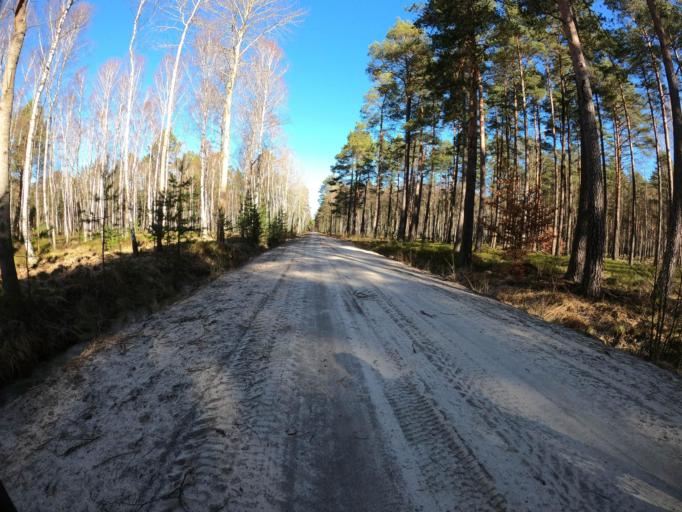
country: PL
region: Greater Poland Voivodeship
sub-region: Powiat zlotowski
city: Sypniewo
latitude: 53.5012
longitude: 16.6415
